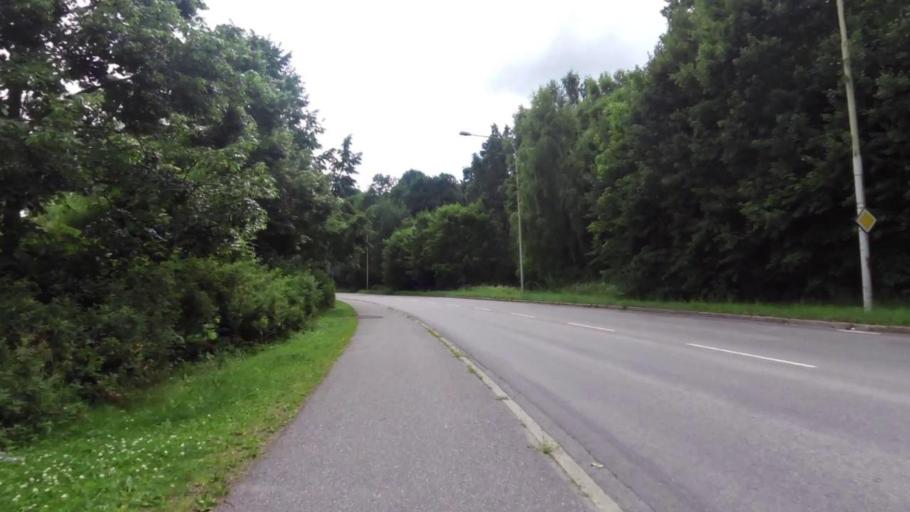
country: SE
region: OEstergoetland
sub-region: Linkopings Kommun
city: Malmslatt
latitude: 58.4120
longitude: 15.5572
